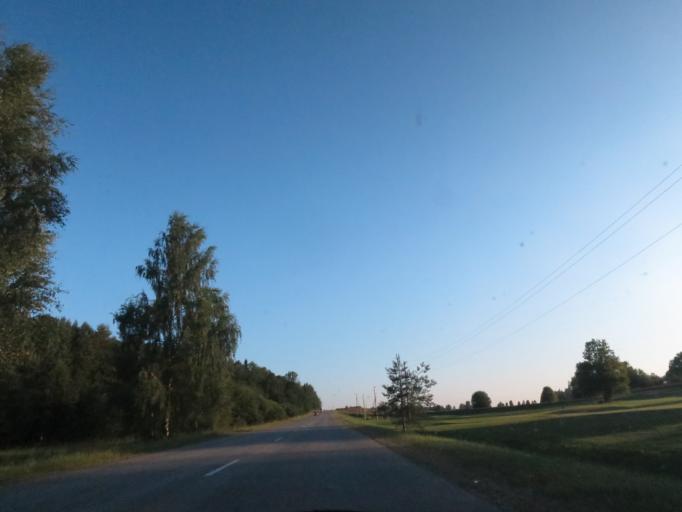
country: LV
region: Sigulda
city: Sigulda
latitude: 57.1756
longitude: 24.8180
